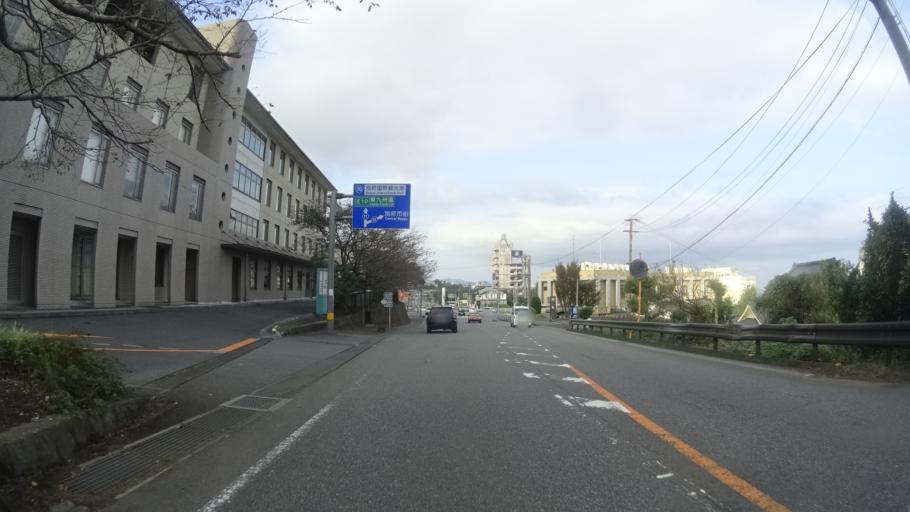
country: JP
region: Oita
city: Beppu
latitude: 33.2900
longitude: 131.4594
